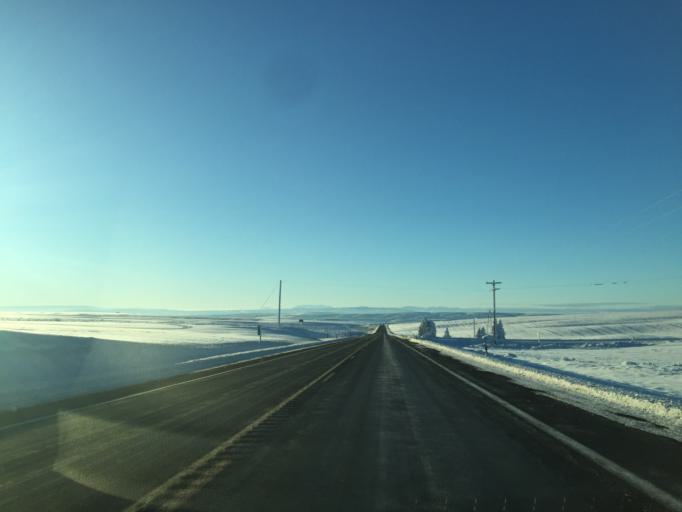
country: US
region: Washington
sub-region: Grant County
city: Soap Lake
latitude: 47.5994
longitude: -119.5750
